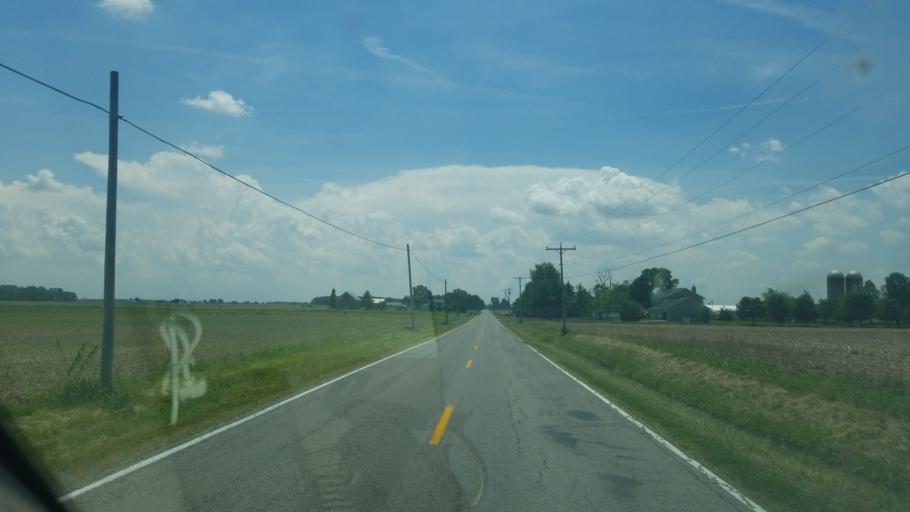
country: US
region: Ohio
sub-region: Hancock County
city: Arlington
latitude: 40.9297
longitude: -83.5945
